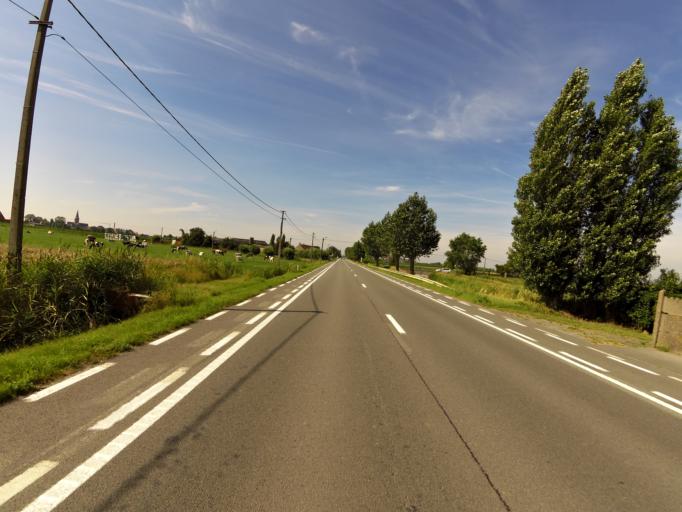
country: BE
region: Flanders
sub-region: Provincie West-Vlaanderen
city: Zuienkerke
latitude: 51.2435
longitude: 3.1129
